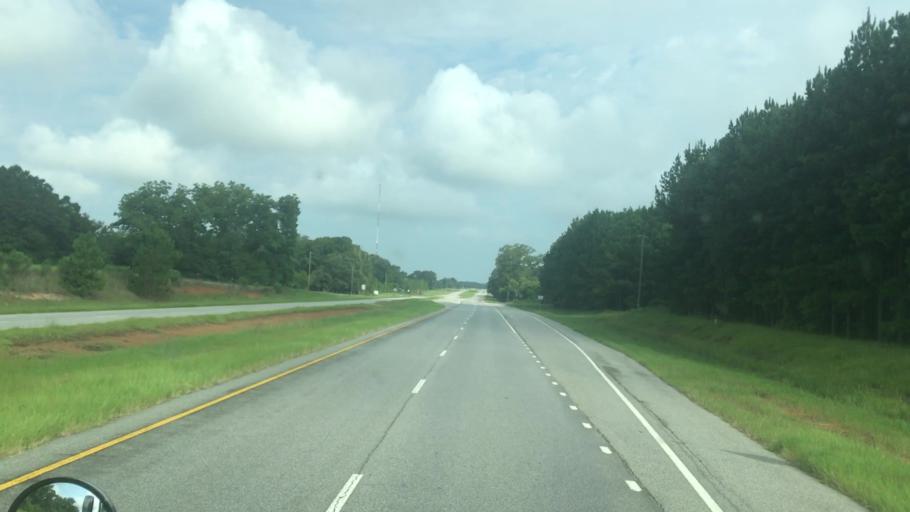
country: US
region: Georgia
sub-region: Miller County
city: Colquitt
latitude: 31.2581
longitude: -84.8089
